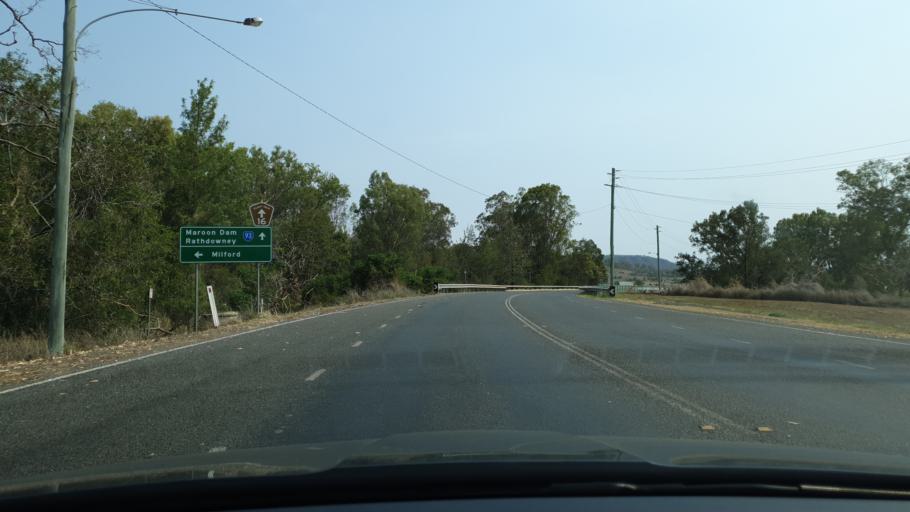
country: AU
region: Queensland
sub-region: Ipswich
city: Deebing Heights
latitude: -28.0068
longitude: 152.6804
